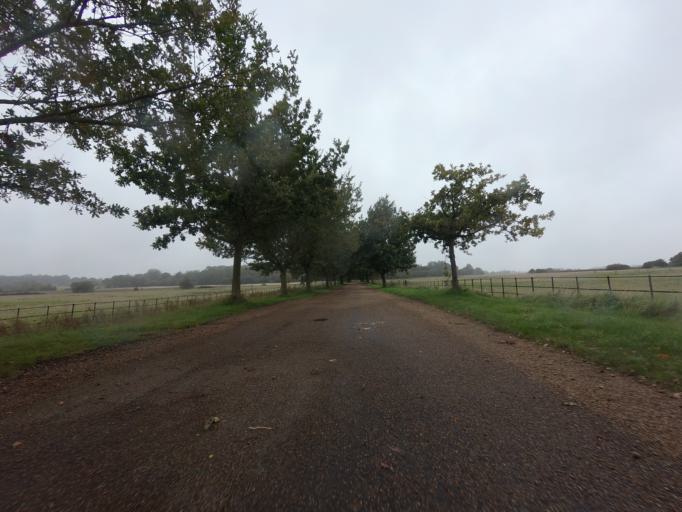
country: GB
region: England
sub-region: Norfolk
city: Dersingham
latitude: 52.8014
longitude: 0.4798
